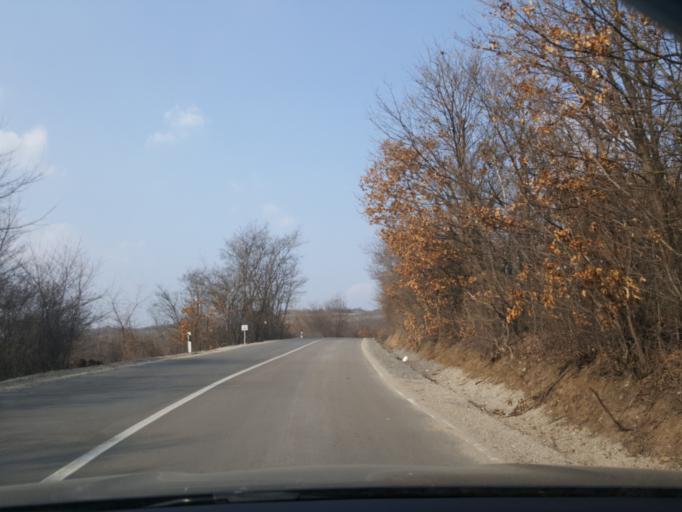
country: RS
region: Central Serbia
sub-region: Nisavski Okrug
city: Aleksinac
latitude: 43.4980
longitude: 21.7636
